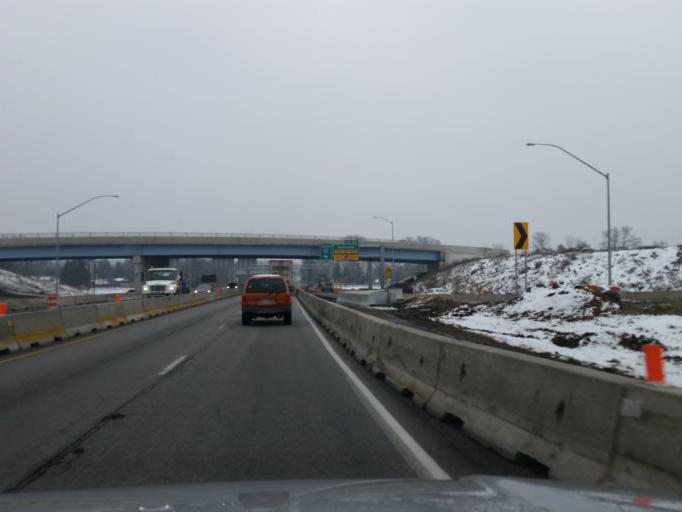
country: US
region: Pennsylvania
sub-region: Cumberland County
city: Lemoyne
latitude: 40.2379
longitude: -76.8948
